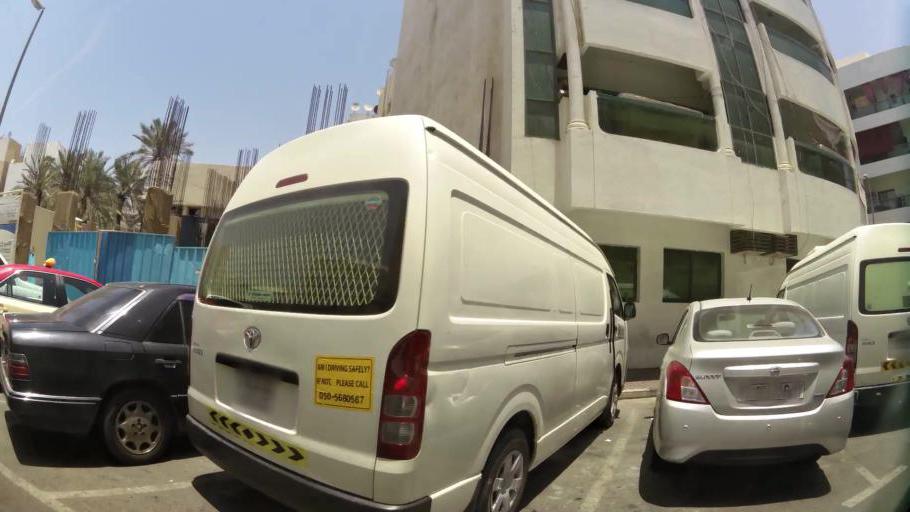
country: AE
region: Ash Shariqah
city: Sharjah
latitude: 25.2809
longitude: 55.3164
